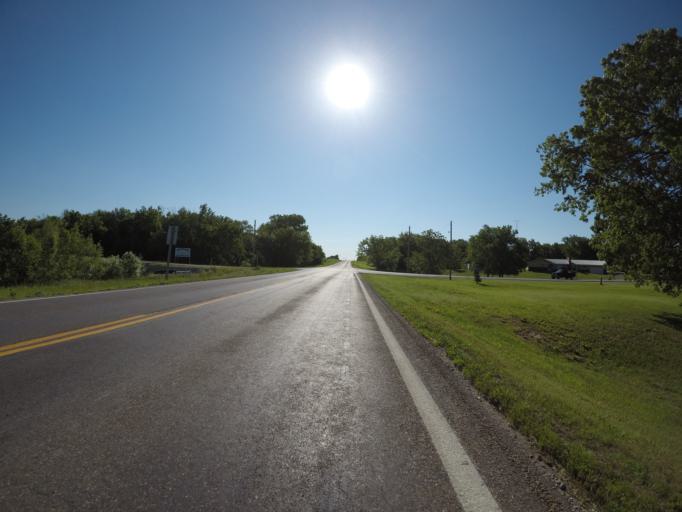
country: US
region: Kansas
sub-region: Lyon County
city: Emporia
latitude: 38.6588
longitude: -96.1704
